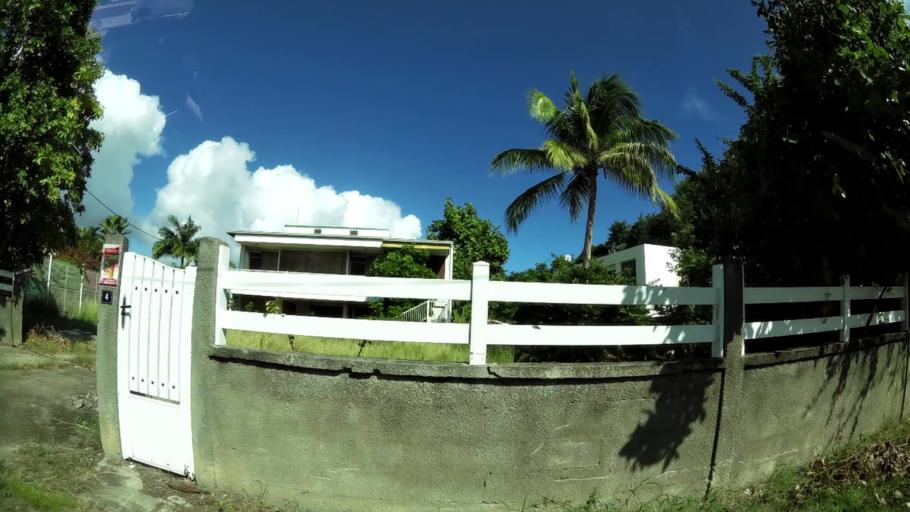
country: GP
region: Guadeloupe
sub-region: Guadeloupe
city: Sainte-Anne
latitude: 16.2293
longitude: -61.3762
